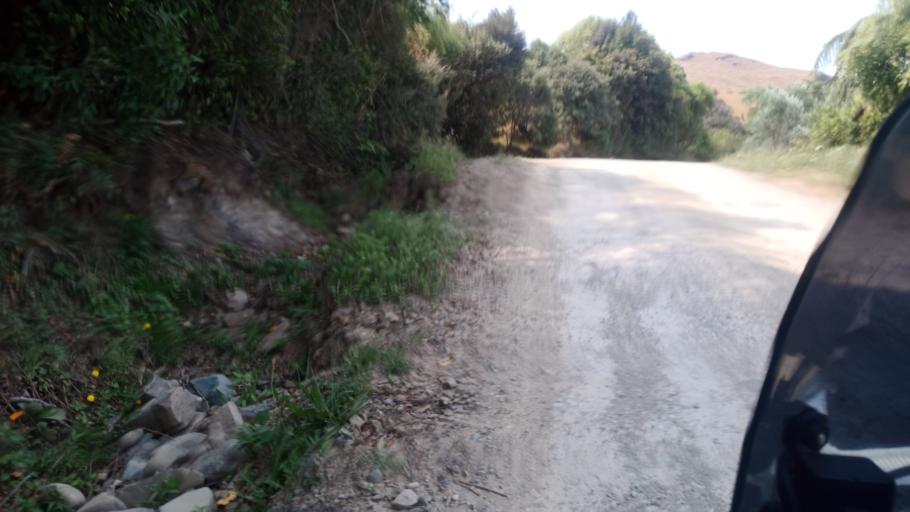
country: NZ
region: Bay of Plenty
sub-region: Opotiki District
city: Opotiki
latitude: -37.6462
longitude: 178.1378
